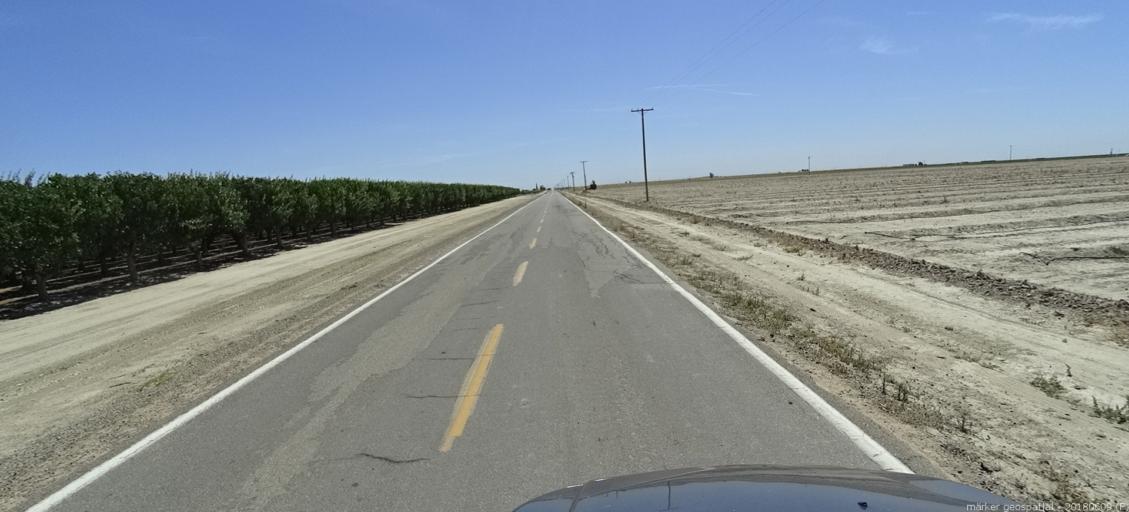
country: US
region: California
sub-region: Fresno County
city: Firebaugh
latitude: 36.9526
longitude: -120.3679
